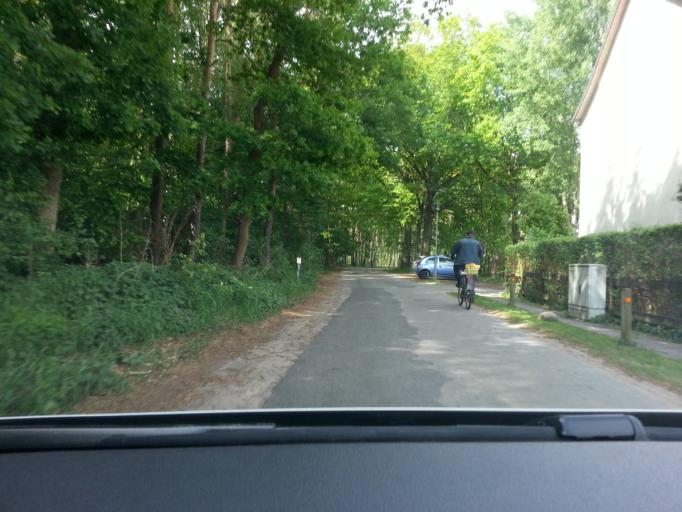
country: DE
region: Mecklenburg-Vorpommern
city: Torgelow
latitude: 53.6401
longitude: 13.9989
